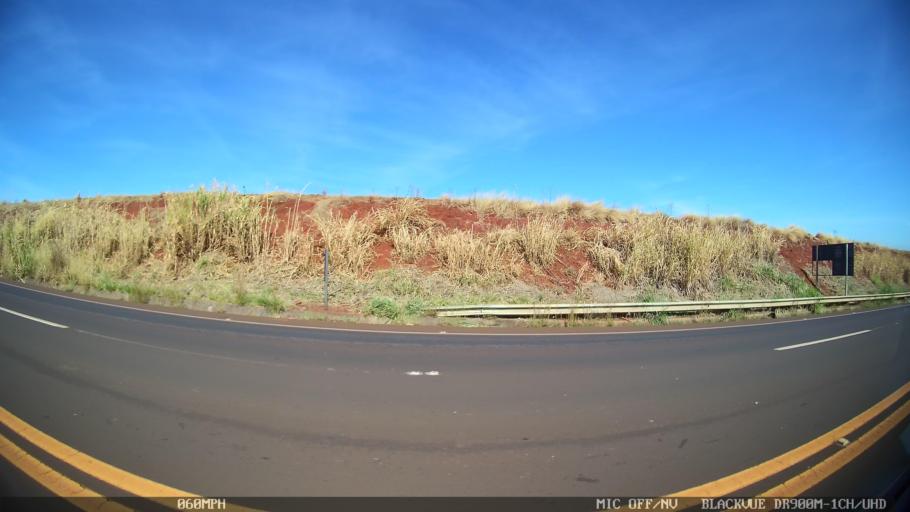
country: BR
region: Sao Paulo
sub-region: Nuporanga
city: Nuporanga
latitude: -20.5607
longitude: -47.6314
